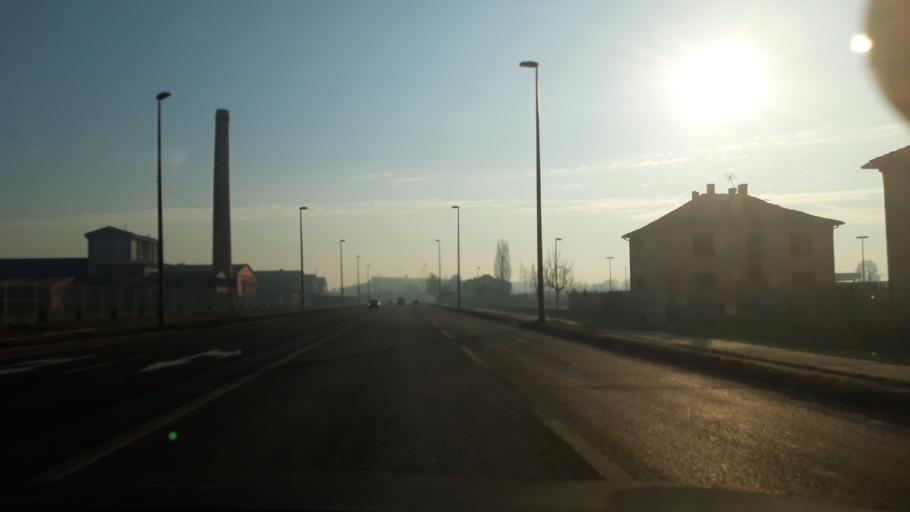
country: RS
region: Central Serbia
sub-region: Macvanski Okrug
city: Sabac
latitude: 44.7478
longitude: 19.7151
